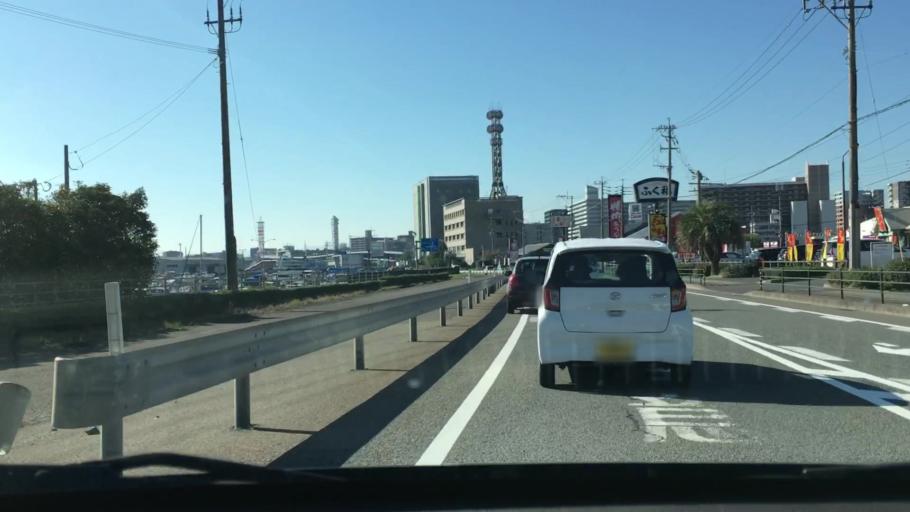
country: JP
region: Kagoshima
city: Kagoshima-shi
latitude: 31.6020
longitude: 130.5664
